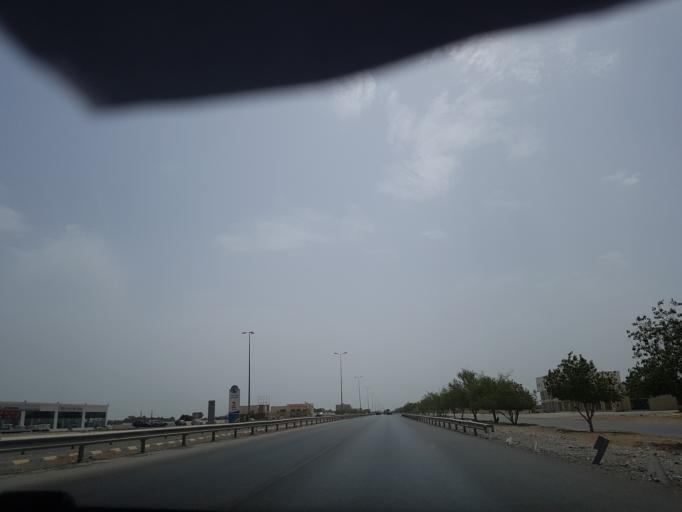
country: OM
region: Al Batinah
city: As Suwayq
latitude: 23.7429
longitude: 57.6290
